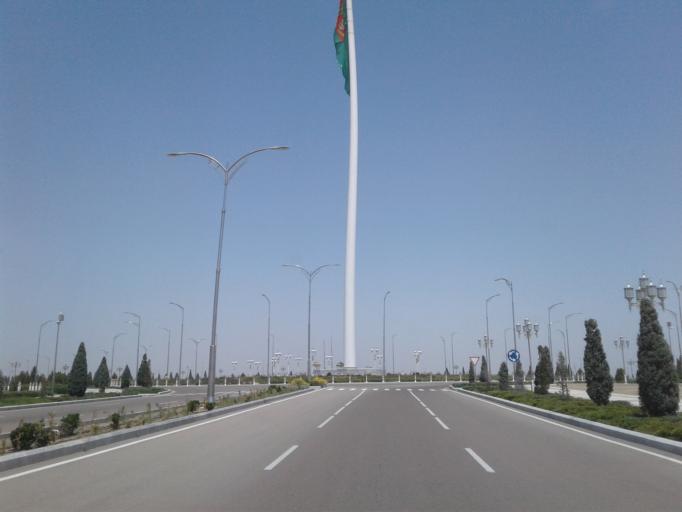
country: TM
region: Balkan
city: Turkmenbasy
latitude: 39.9581
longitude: 52.8633
